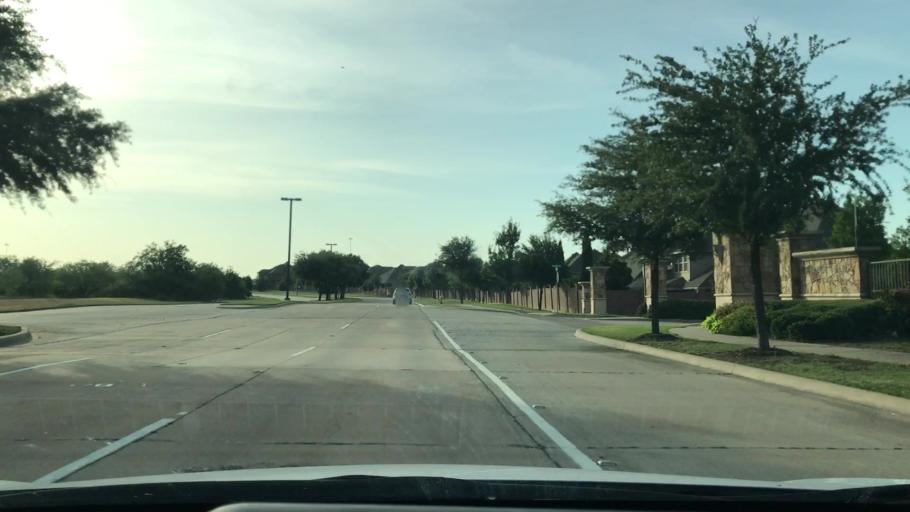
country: US
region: Texas
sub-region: Dallas County
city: Farmers Branch
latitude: 32.9035
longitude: -96.9472
